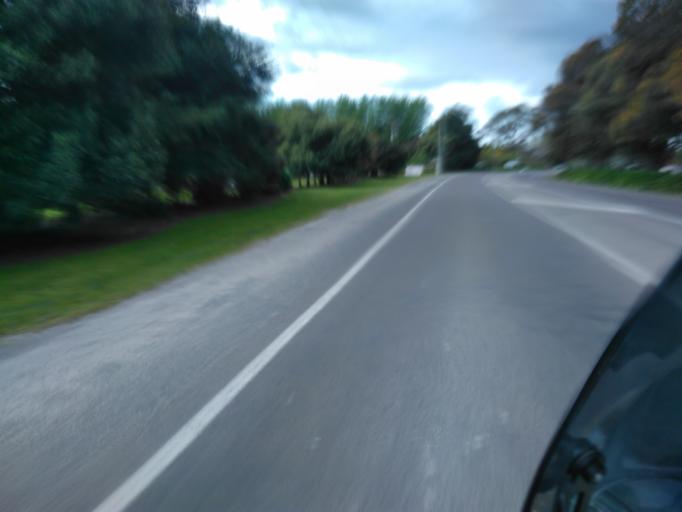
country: NZ
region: Gisborne
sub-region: Gisborne District
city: Gisborne
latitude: -38.6486
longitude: 177.9813
